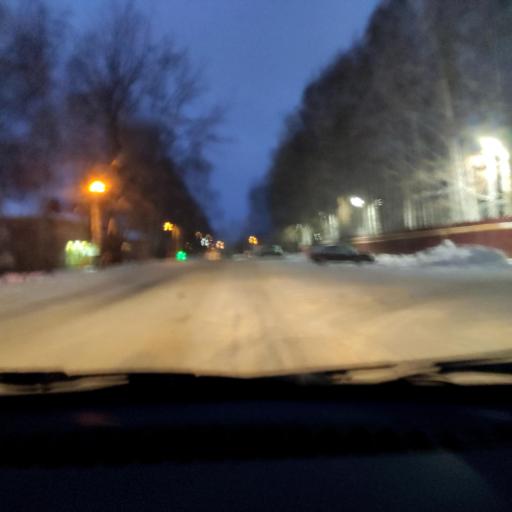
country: RU
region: Bashkortostan
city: Blagoveshchensk
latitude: 55.0502
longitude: 55.9504
